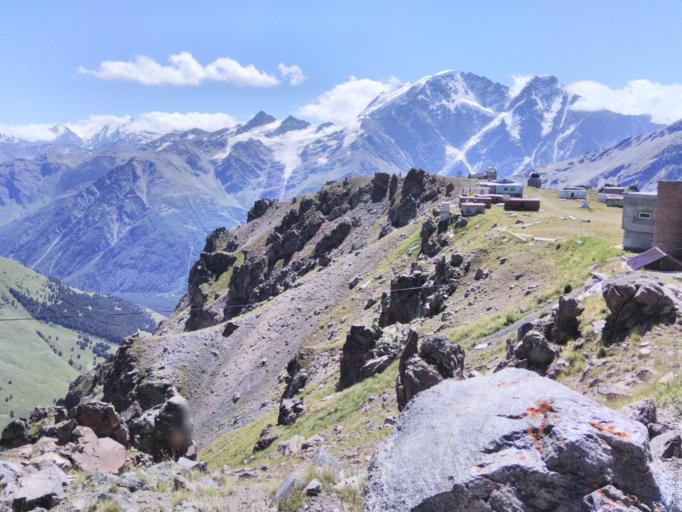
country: RU
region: Kabardino-Balkariya
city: Terskol
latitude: 43.2778
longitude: 42.5002
